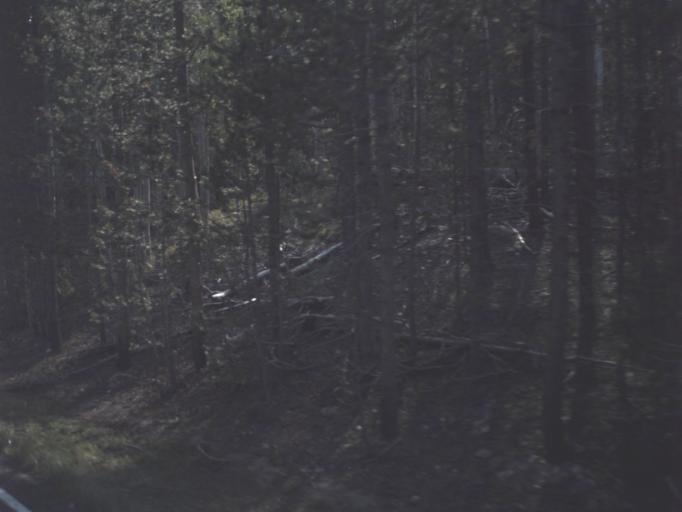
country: US
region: Utah
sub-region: Summit County
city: Oakley
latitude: 40.8096
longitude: -110.8741
